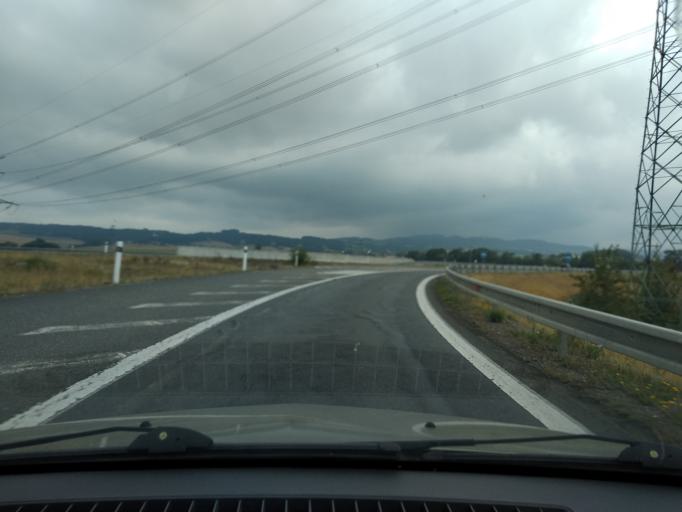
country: CZ
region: Olomoucky
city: Postrelmov
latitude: 49.8948
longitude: 16.8953
